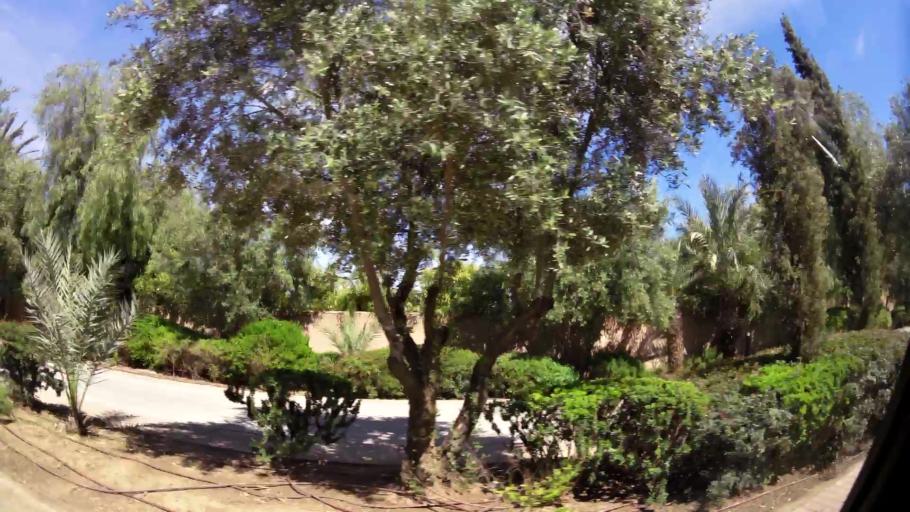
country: MA
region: Marrakech-Tensift-Al Haouz
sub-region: Marrakech
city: Marrakesh
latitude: 31.6026
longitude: -7.9532
